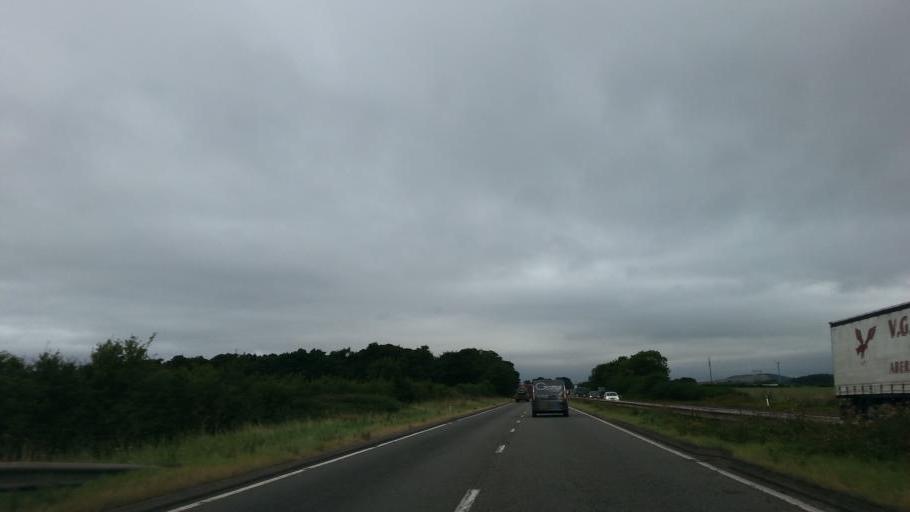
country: GB
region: England
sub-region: Nottinghamshire
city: Bircotes
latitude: 53.3613
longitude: -1.0486
